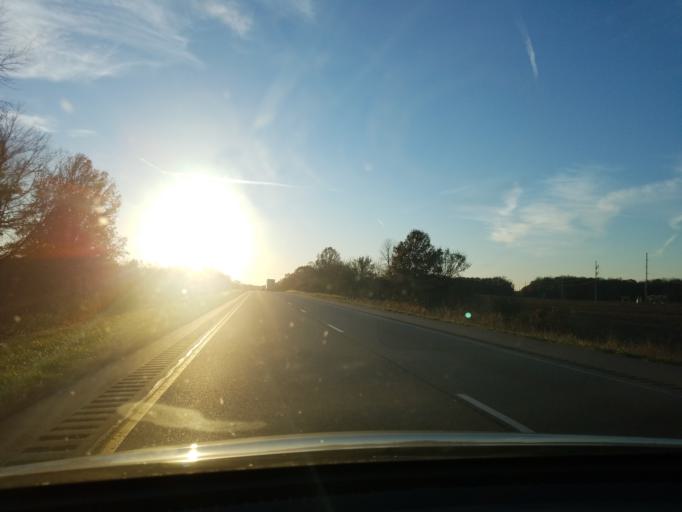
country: US
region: Indiana
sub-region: Warrick County
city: Chandler
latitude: 38.1802
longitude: -87.4027
